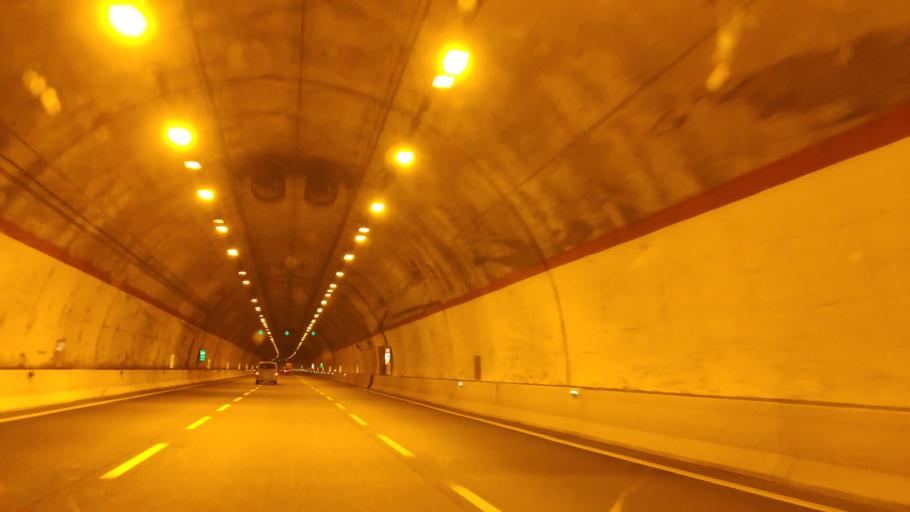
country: IT
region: Campania
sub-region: Provincia di Salerno
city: Contursi Terme
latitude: 40.6210
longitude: 15.2427
